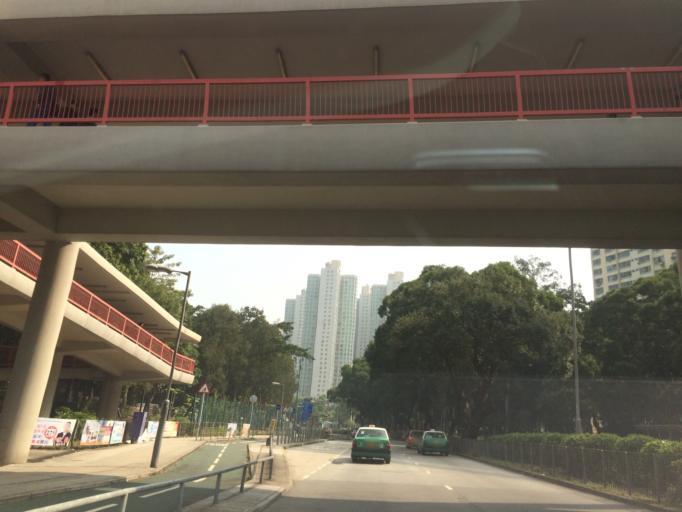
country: HK
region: Tai Po
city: Tai Po
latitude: 22.4567
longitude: 114.1698
